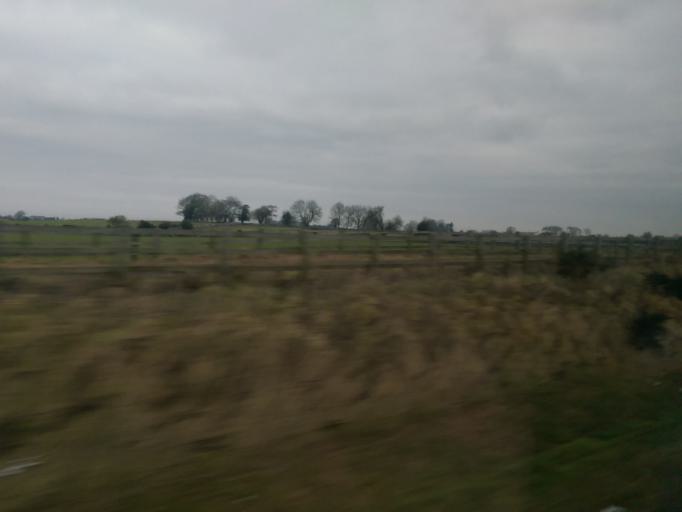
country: IE
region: Connaught
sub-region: County Galway
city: Ballinasloe
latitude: 53.3244
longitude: -8.1418
